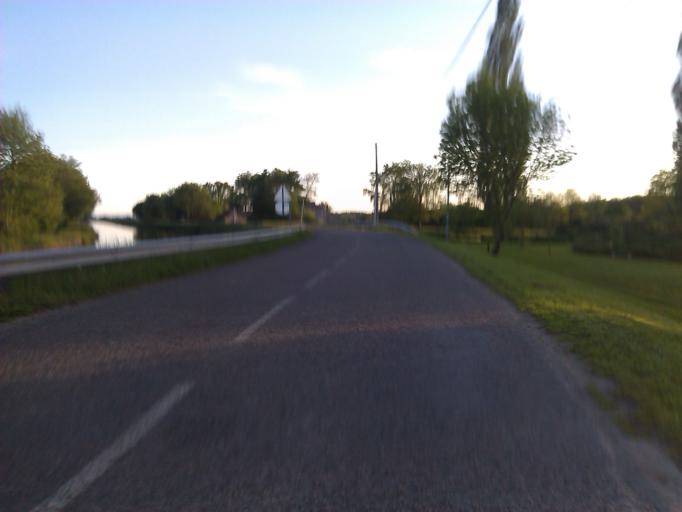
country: FR
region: Bourgogne
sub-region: Departement de Saone-et-Loire
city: Palinges
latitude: 46.5290
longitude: 4.2009
